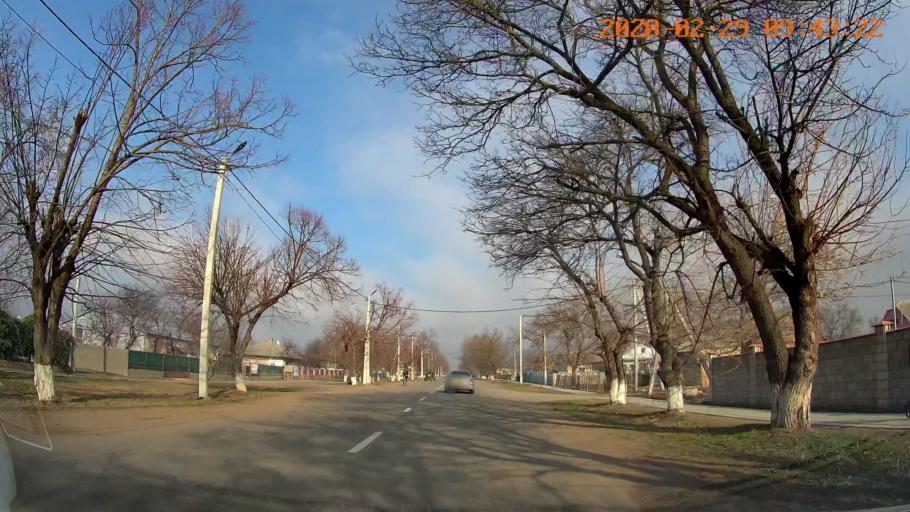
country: MD
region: Telenesti
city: Crasnoe
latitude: 46.6438
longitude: 29.8221
